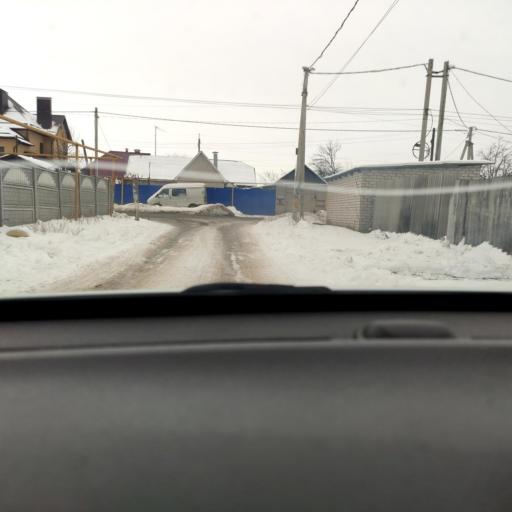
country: RU
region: Voronezj
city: Volya
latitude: 51.7507
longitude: 39.4986
